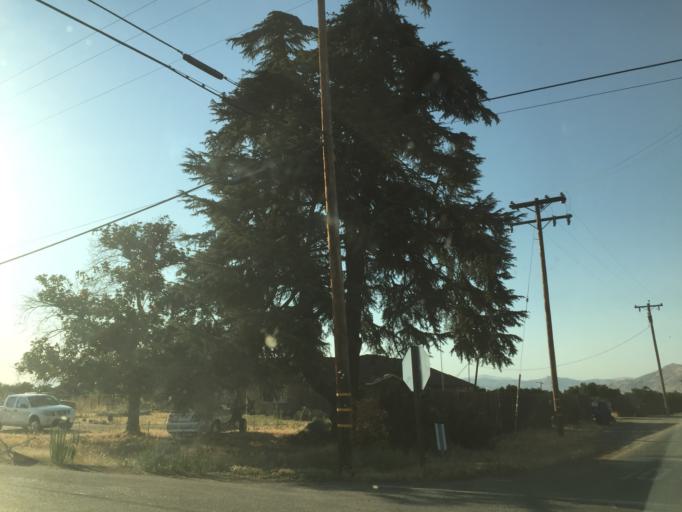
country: US
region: California
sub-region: Fresno County
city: Orange Cove
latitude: 36.6241
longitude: -119.2869
